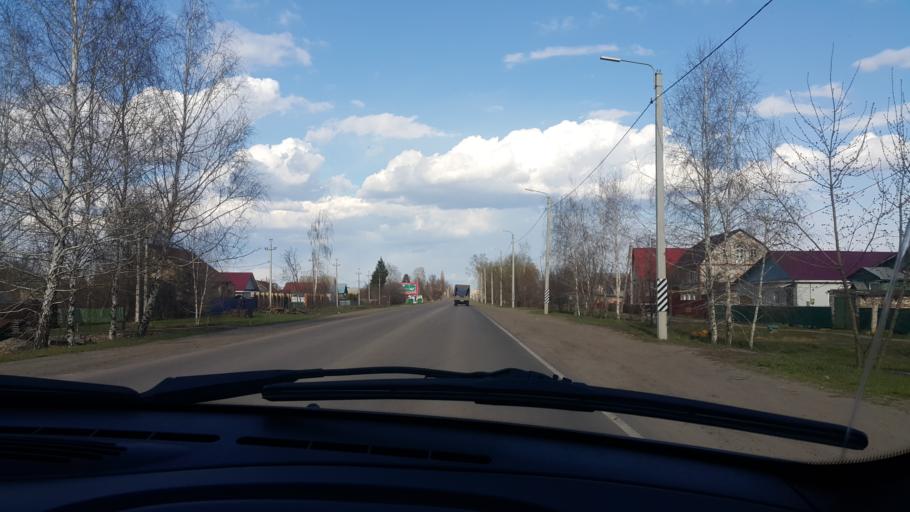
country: RU
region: Tambov
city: Zavoronezhskoye
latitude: 52.8854
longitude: 40.5538
